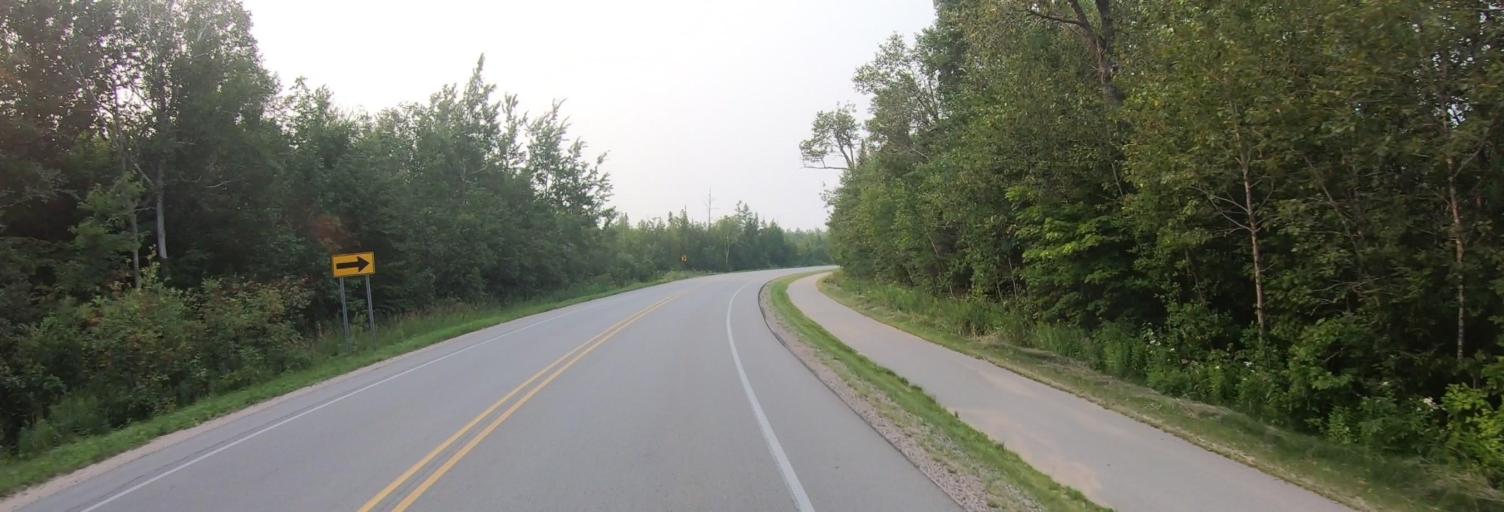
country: US
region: Michigan
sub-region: Chippewa County
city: Sault Ste. Marie
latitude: 46.4311
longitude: -84.6100
